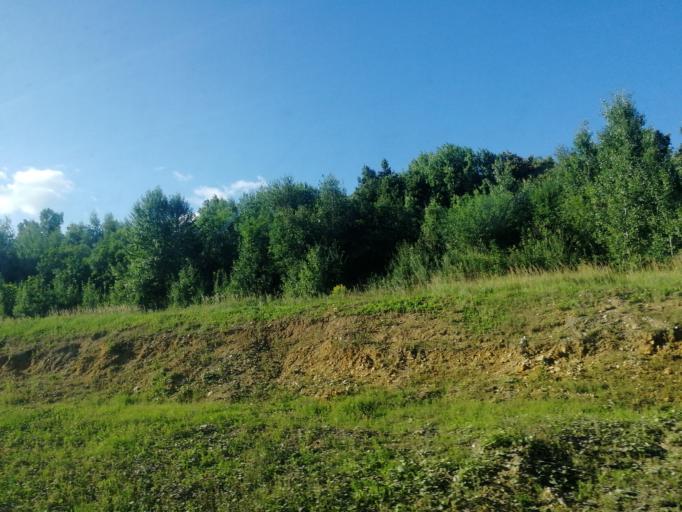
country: RU
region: Tula
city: Novogurovskiy
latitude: 54.2780
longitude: 37.2449
